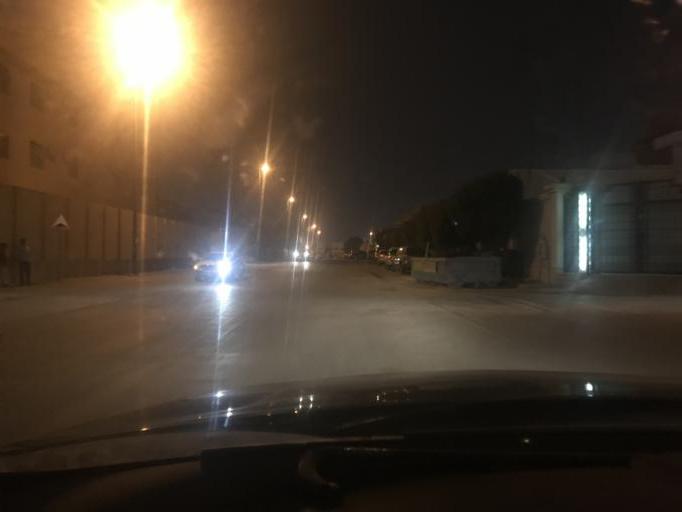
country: SA
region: Ar Riyad
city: Riyadh
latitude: 24.7494
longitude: 46.7767
